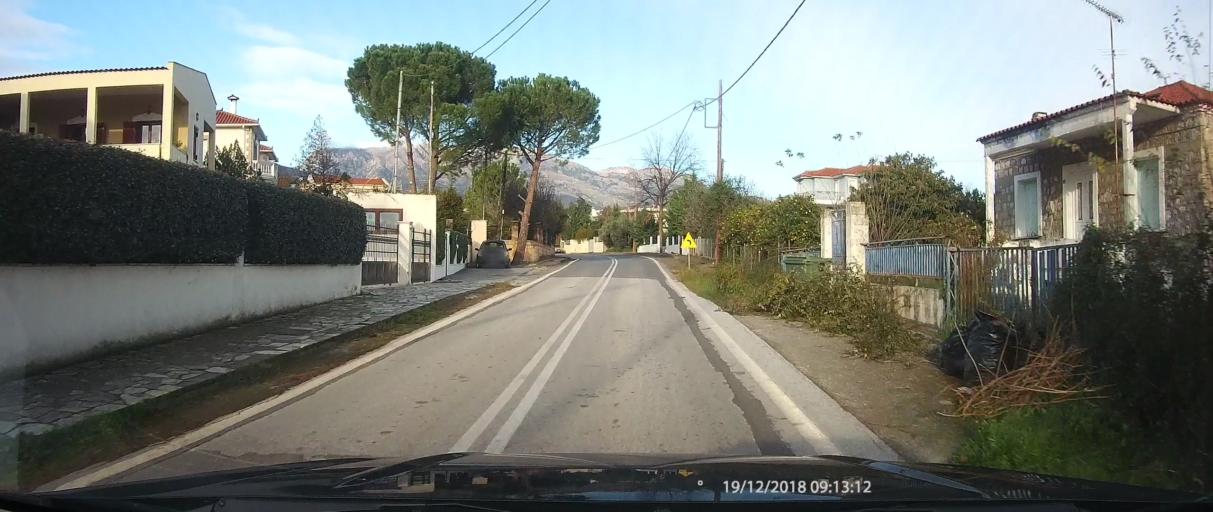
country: GR
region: Peloponnese
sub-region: Nomos Lakonias
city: Magoula
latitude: 37.0807
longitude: 22.3999
